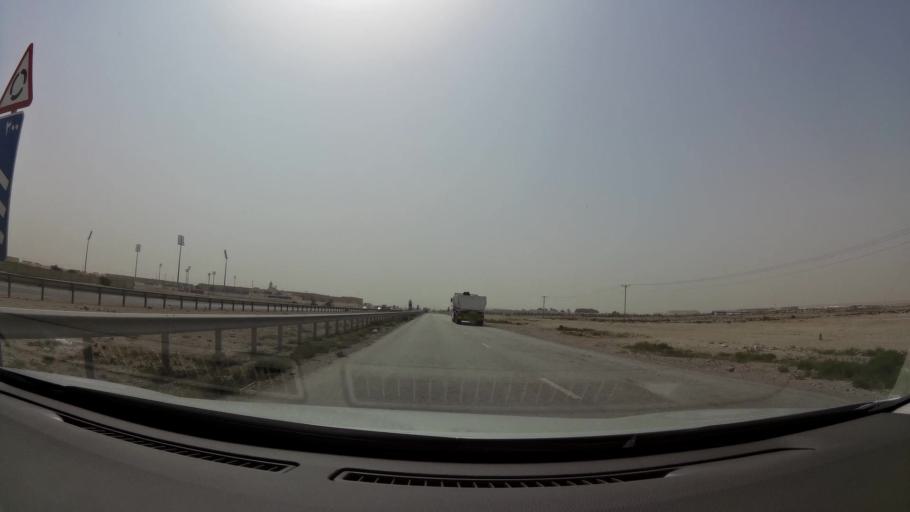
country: QA
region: Baladiyat ar Rayyan
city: Ar Rayyan
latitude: 25.2190
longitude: 51.3579
